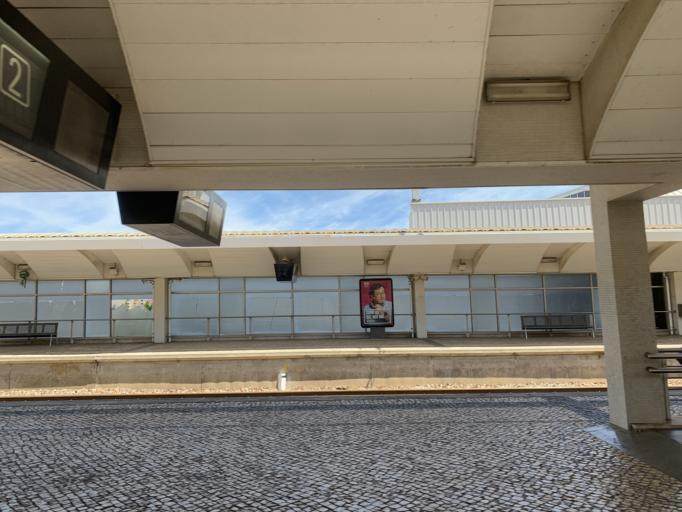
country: PT
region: Lisbon
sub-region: Amadora
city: Amadora
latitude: 38.7513
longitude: -9.2233
